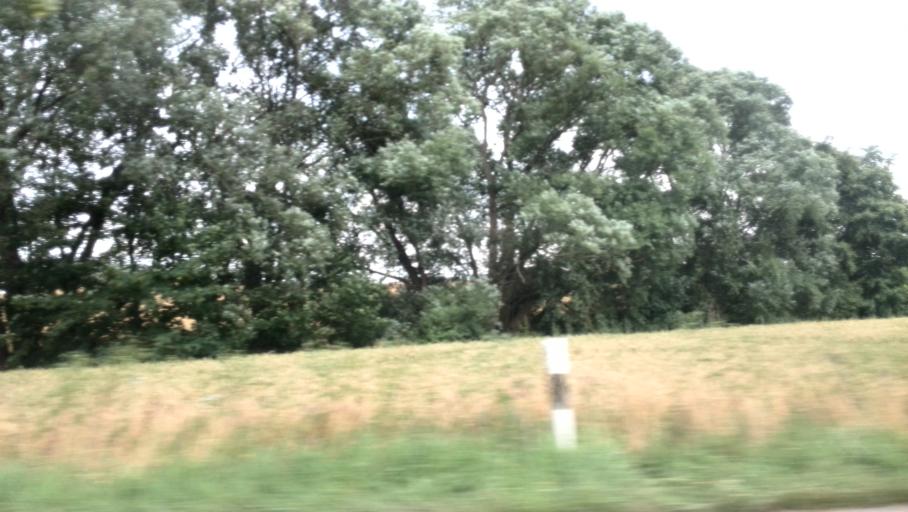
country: DE
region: Lower Saxony
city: Haverlah
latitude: 52.0782
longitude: 10.1731
